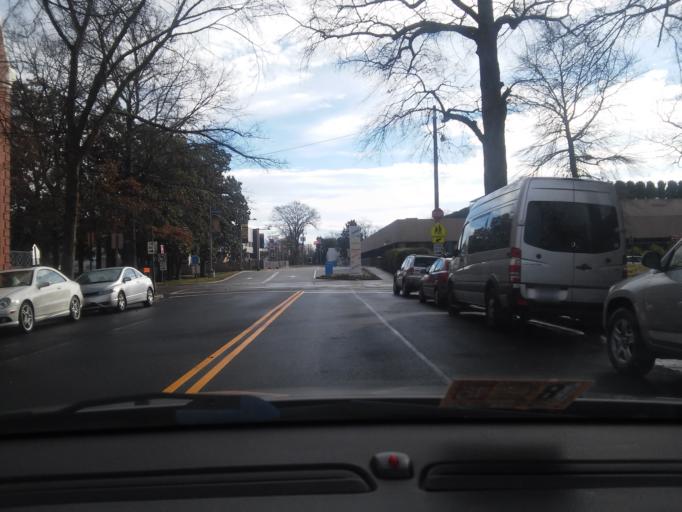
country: US
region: Virginia
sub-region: City of Richmond
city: Richmond
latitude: 37.5582
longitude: -77.4761
